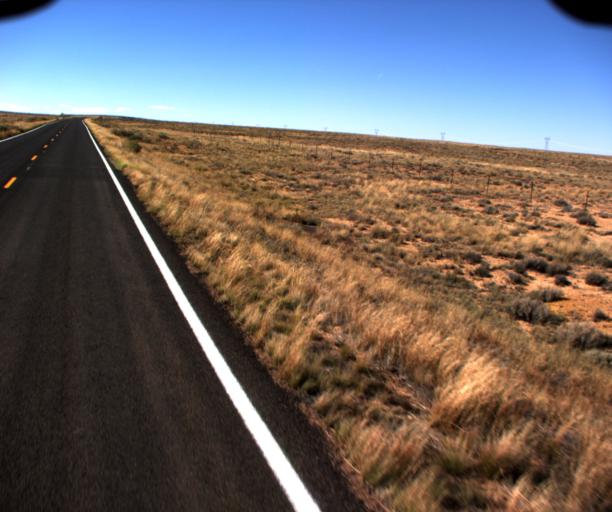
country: US
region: Arizona
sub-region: Navajo County
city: First Mesa
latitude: 35.9702
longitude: -110.7954
